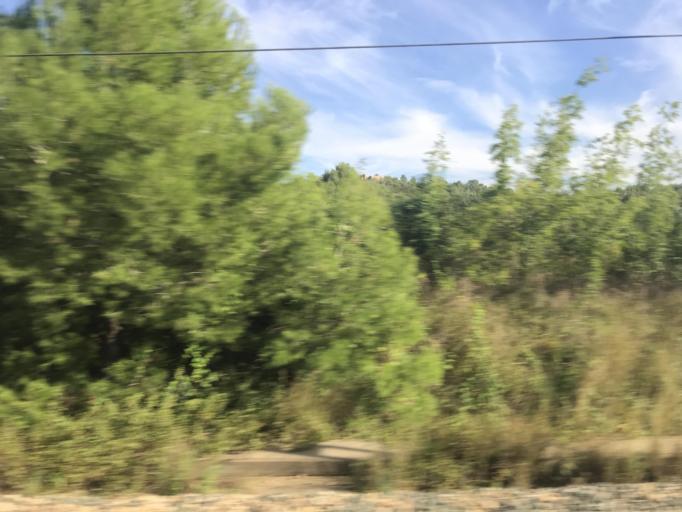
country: ES
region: Catalonia
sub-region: Provincia de Tarragona
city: Ulldecona
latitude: 40.5916
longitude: 0.4449
